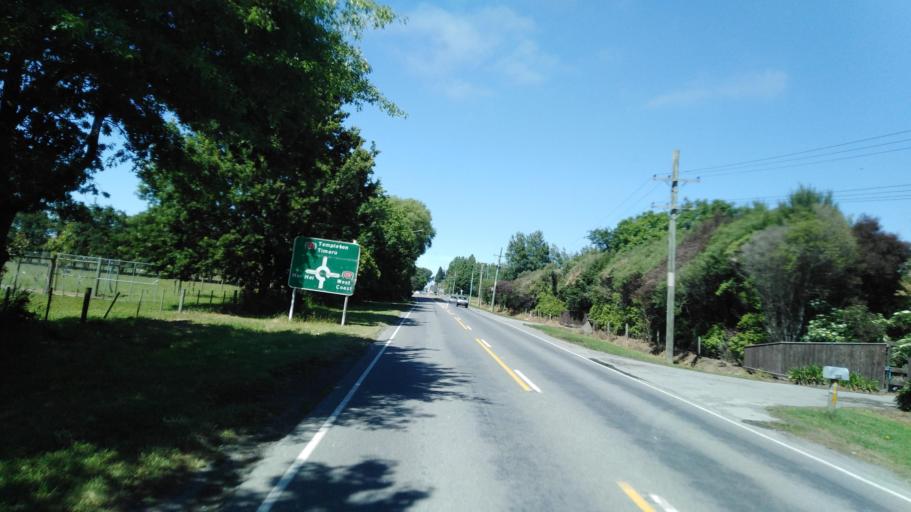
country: NZ
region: Canterbury
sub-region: Selwyn District
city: Prebbleton
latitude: -43.5178
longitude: 172.5059
